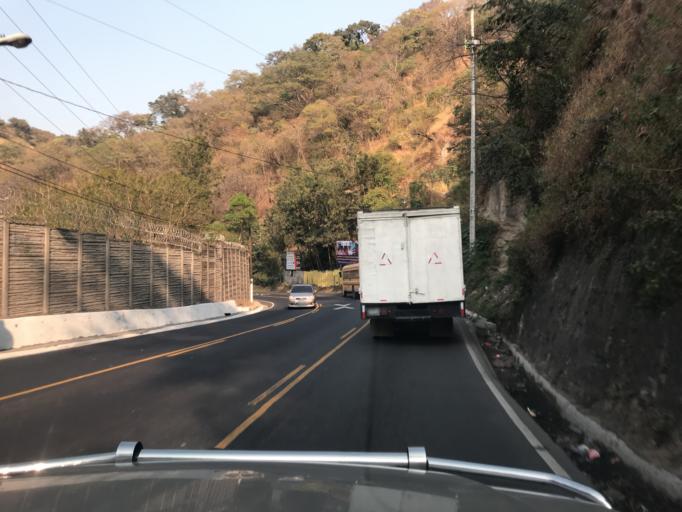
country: GT
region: Guatemala
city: Santa Catarina Pinula
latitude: 14.5572
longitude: -90.5260
